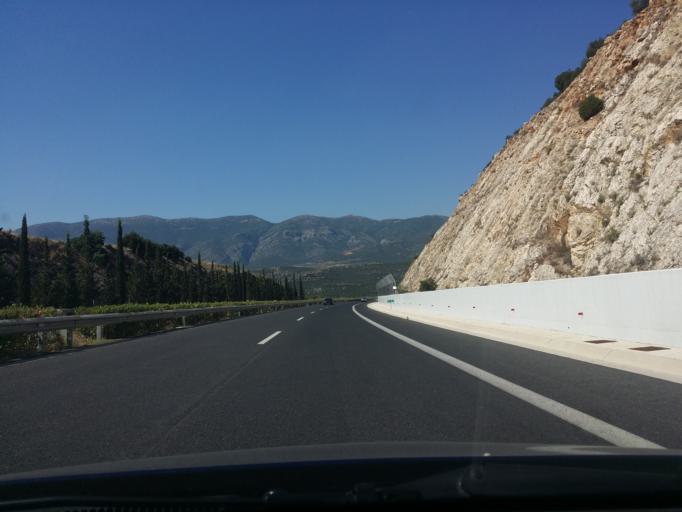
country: GR
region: Peloponnese
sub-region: Nomos Korinthias
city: Nemea
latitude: 37.7301
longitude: 22.6220
